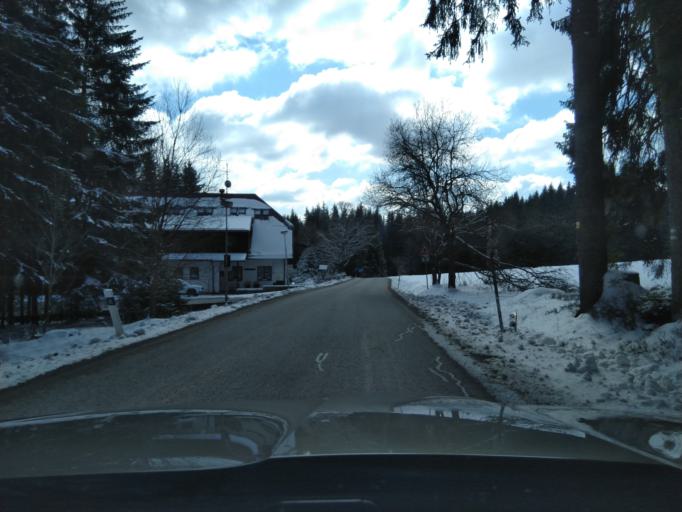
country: CZ
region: Jihocesky
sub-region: Okres Prachatice
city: Zdikov
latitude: 49.0494
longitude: 13.6628
